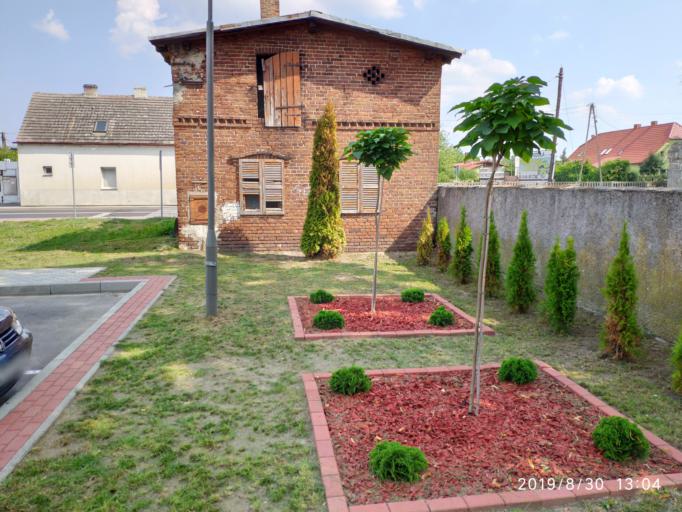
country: PL
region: Lubusz
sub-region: Powiat krosnienski
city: Dabie
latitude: 52.0107
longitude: 15.1516
